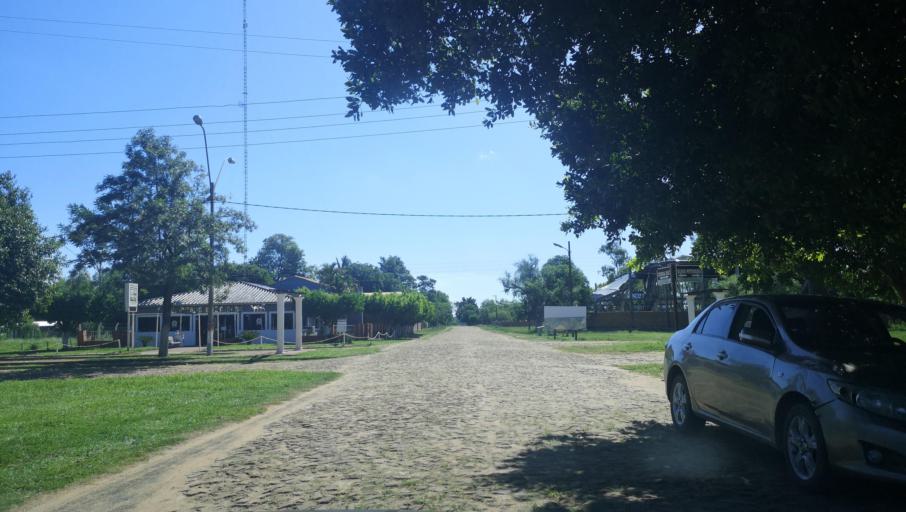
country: PY
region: Caaguazu
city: Carayao
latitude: -25.1952
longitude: -56.3993
